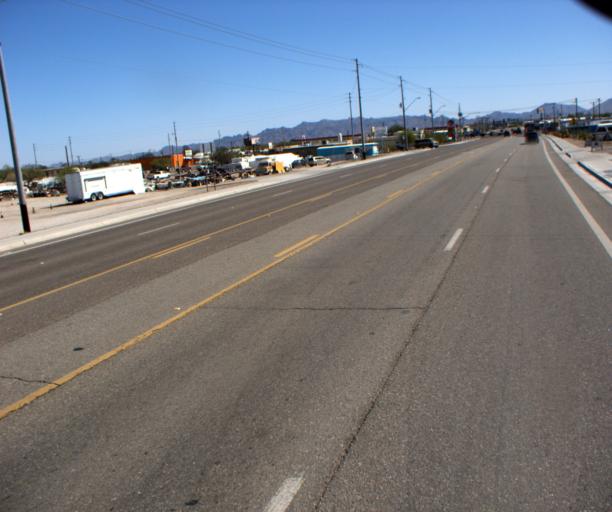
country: US
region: Arizona
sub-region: La Paz County
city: Quartzsite
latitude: 33.6662
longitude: -114.2201
